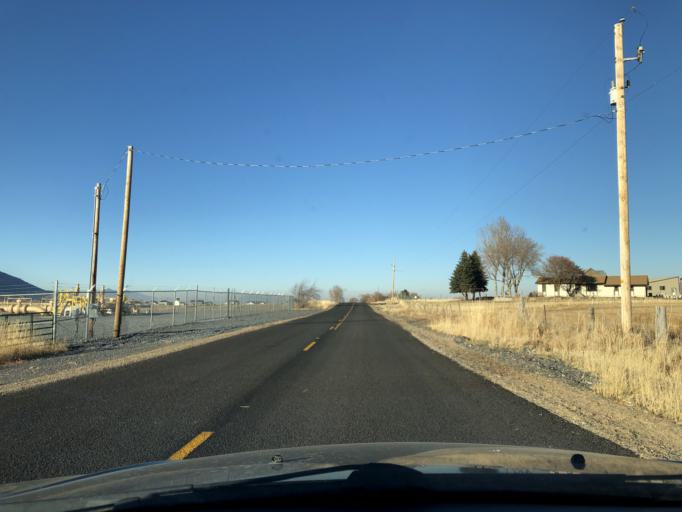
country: US
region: Utah
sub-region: Cache County
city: Wellsville
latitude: 41.6012
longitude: -111.9298
